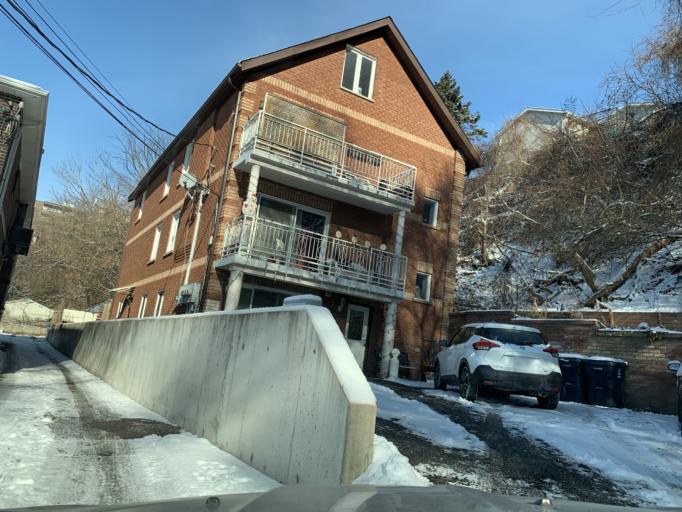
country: CA
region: Ontario
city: Toronto
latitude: 43.6766
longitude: -79.4814
